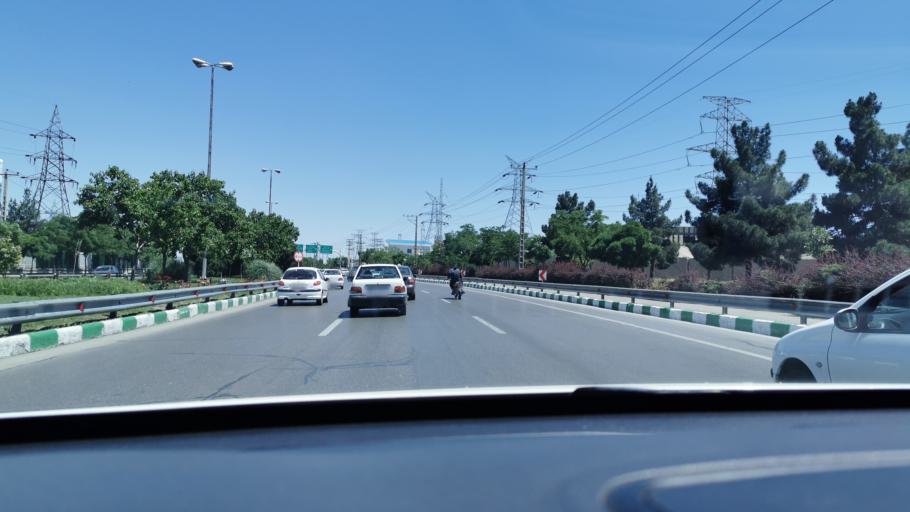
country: IR
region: Razavi Khorasan
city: Mashhad
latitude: 36.2574
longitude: 59.5899
